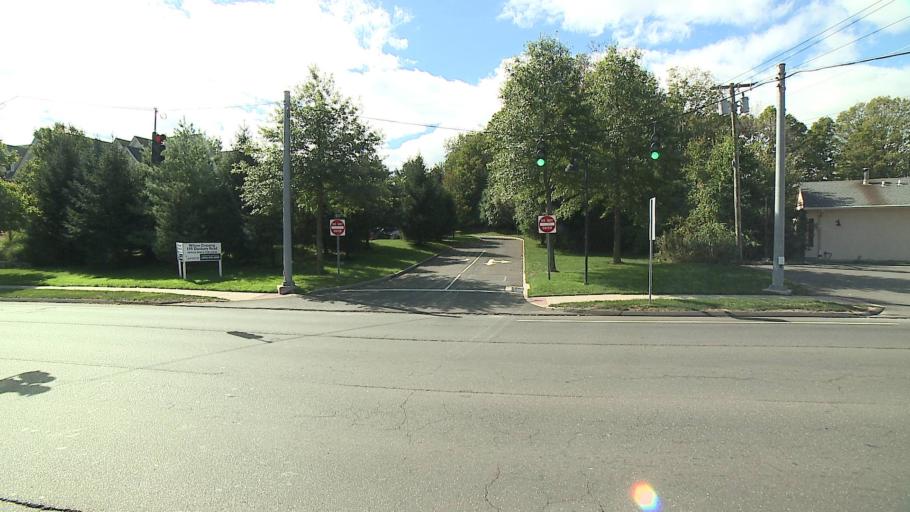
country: US
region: Connecticut
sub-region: Fairfield County
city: Wilton
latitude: 41.1860
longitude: -73.4219
